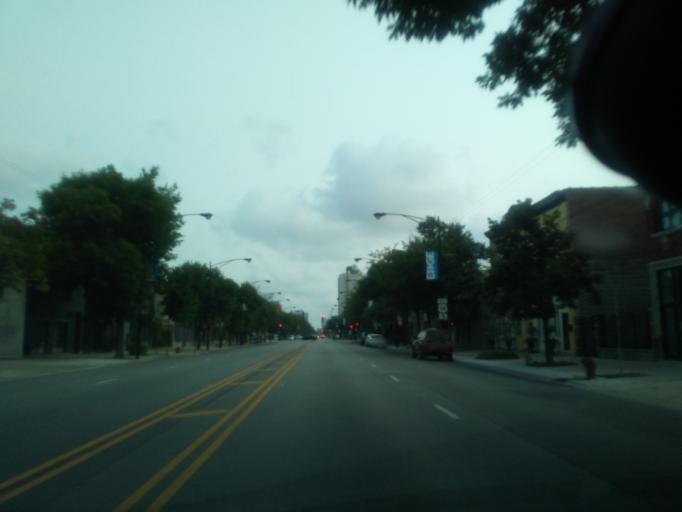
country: US
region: Illinois
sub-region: Cook County
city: Evanston
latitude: 41.9822
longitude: -87.6600
